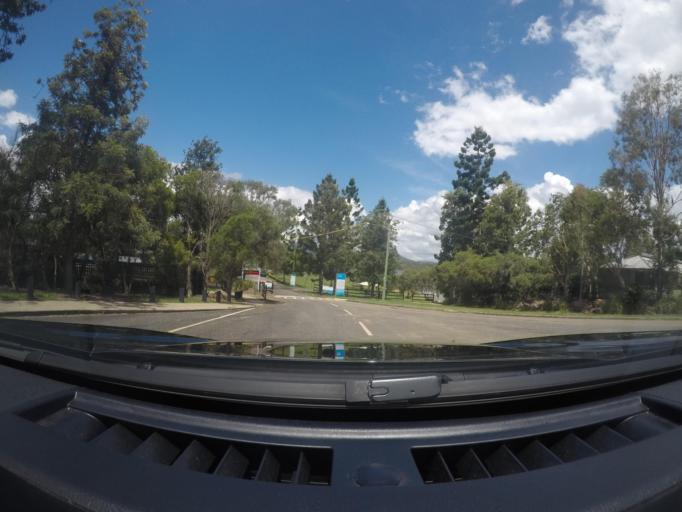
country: AU
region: Queensland
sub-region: Moreton Bay
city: Woodford
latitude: -27.1032
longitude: 152.5609
